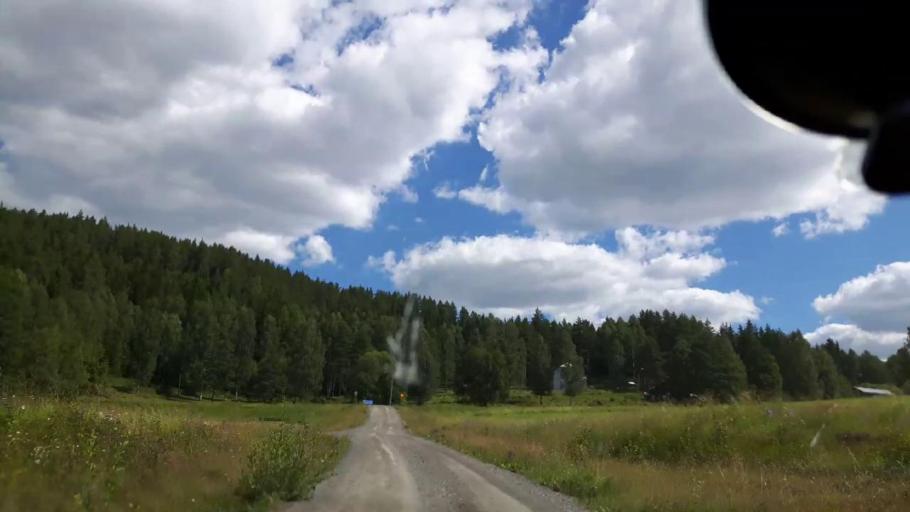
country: SE
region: Jaemtland
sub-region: Ragunda Kommun
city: Hammarstrand
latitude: 62.9554
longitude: 16.6811
